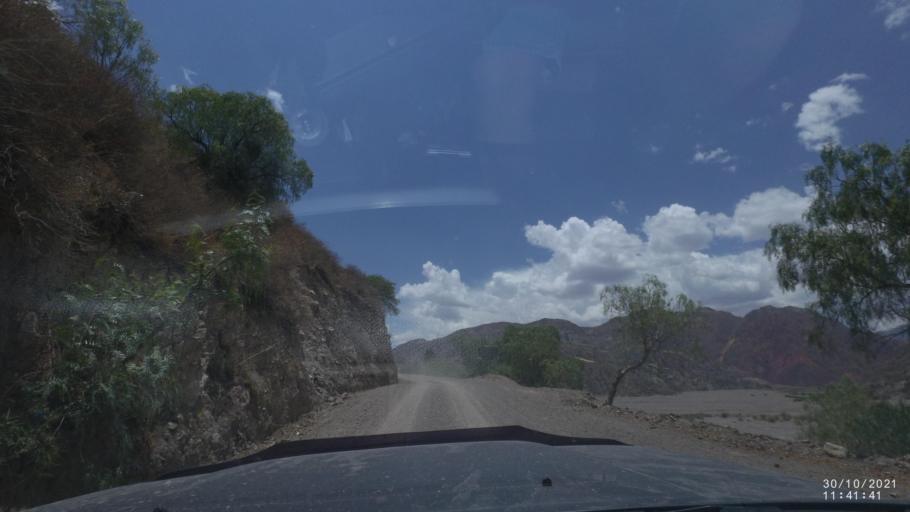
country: BO
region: Cochabamba
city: Colchani
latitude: -17.5164
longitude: -66.6229
